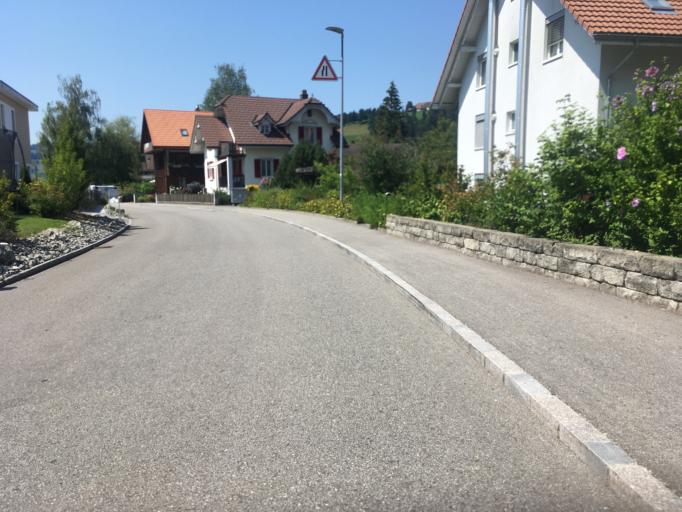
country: CH
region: Bern
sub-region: Emmental District
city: Langnau
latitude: 46.9405
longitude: 7.7758
